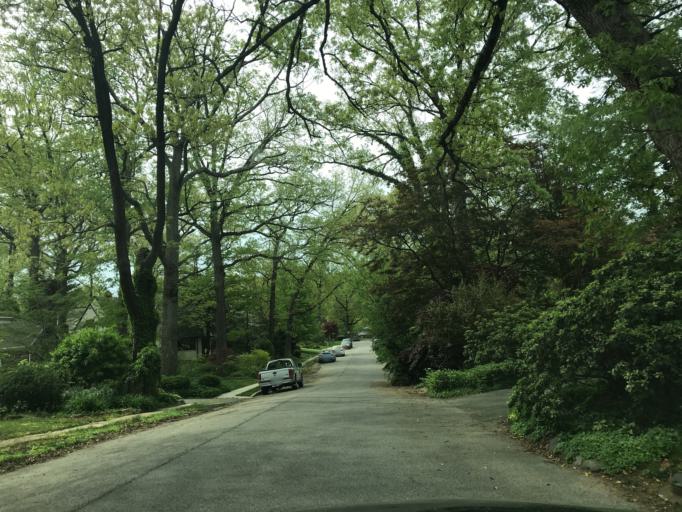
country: US
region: Maryland
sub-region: Baltimore County
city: Catonsville
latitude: 39.2621
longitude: -76.7476
